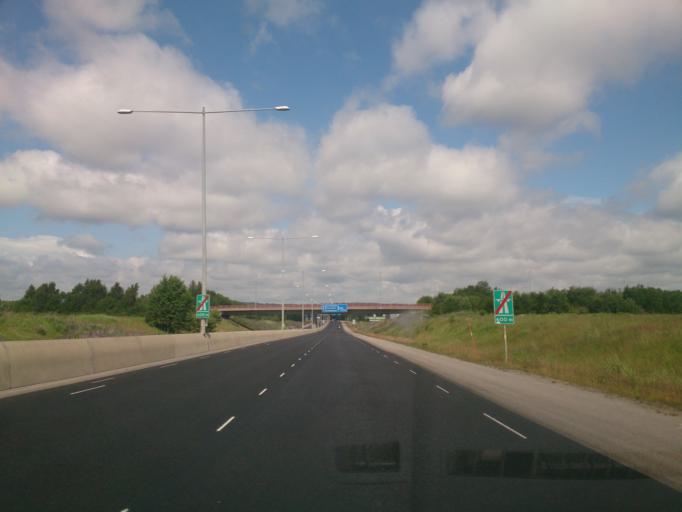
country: SE
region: OEstergoetland
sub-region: Norrkopings Kommun
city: Jursla
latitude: 58.6482
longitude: 16.1654
